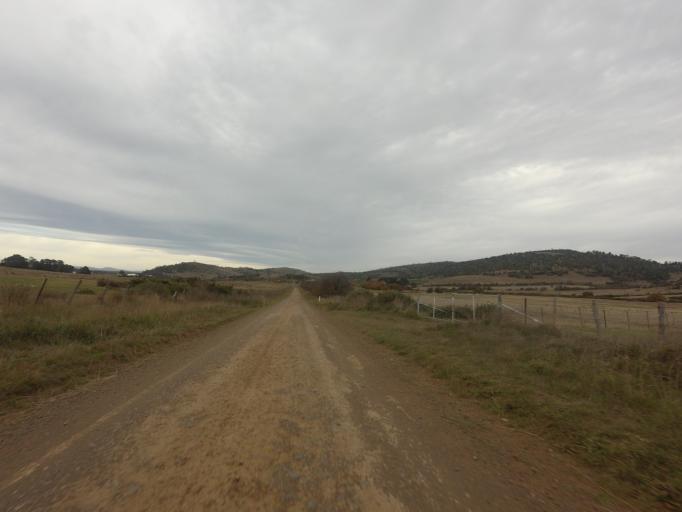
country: AU
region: Tasmania
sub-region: Derwent Valley
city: New Norfolk
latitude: -42.5362
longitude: 146.9428
